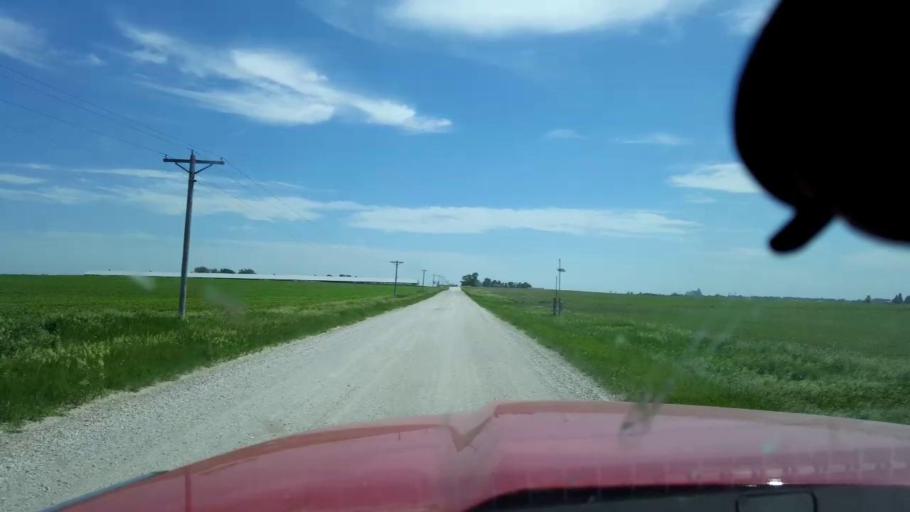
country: US
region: Iowa
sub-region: Hamilton County
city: Jewell
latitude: 42.3478
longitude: -93.5604
